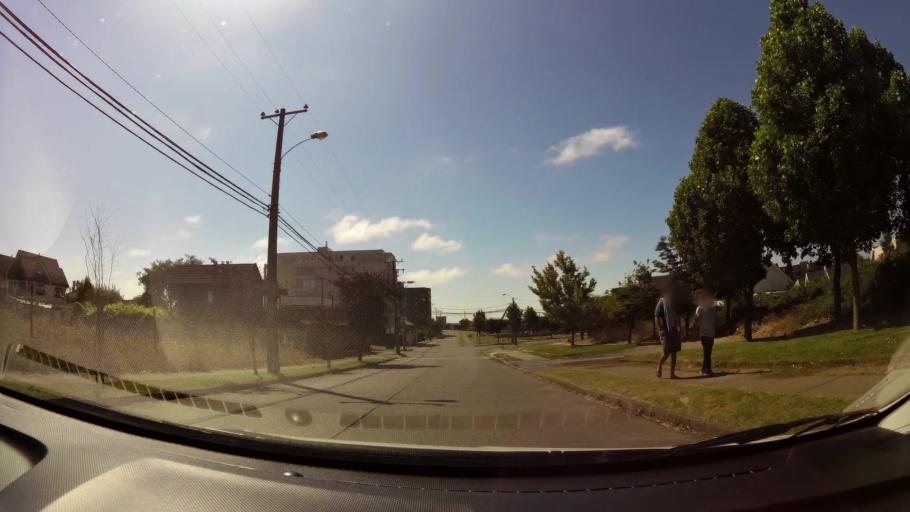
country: CL
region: Biobio
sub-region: Provincia de Concepcion
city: Concepcion
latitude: -36.7832
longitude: -73.0452
